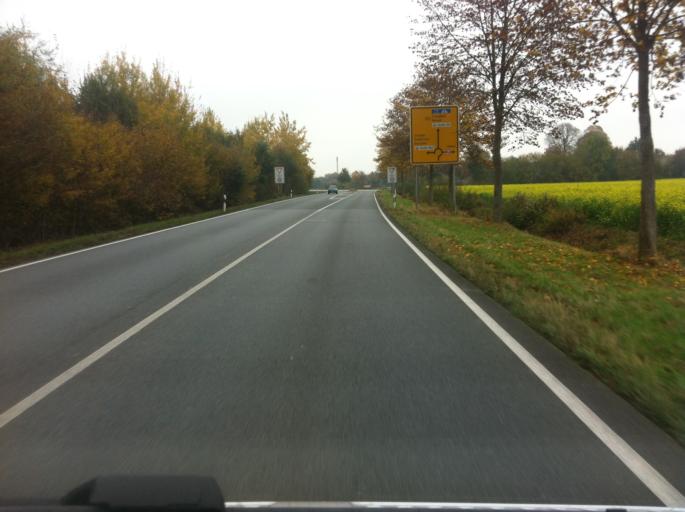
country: DE
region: North Rhine-Westphalia
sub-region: Regierungsbezirk Munster
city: Gescher
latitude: 51.9401
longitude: 6.9812
